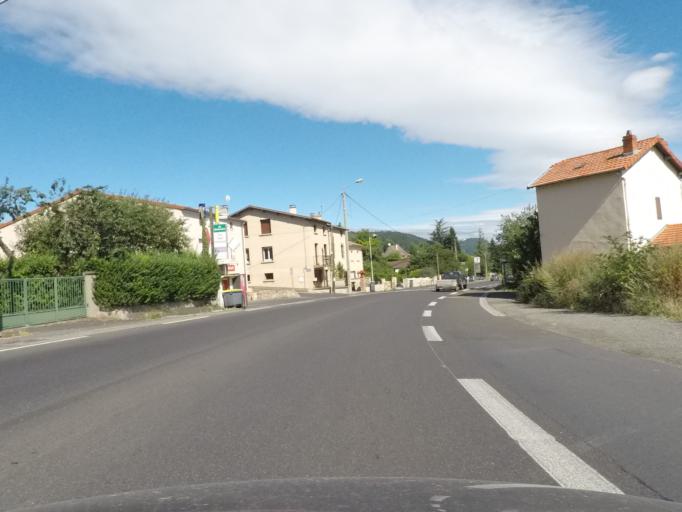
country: FR
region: Auvergne
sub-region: Departement du Puy-de-Dome
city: Ceyrat
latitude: 45.7138
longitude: 3.0705
